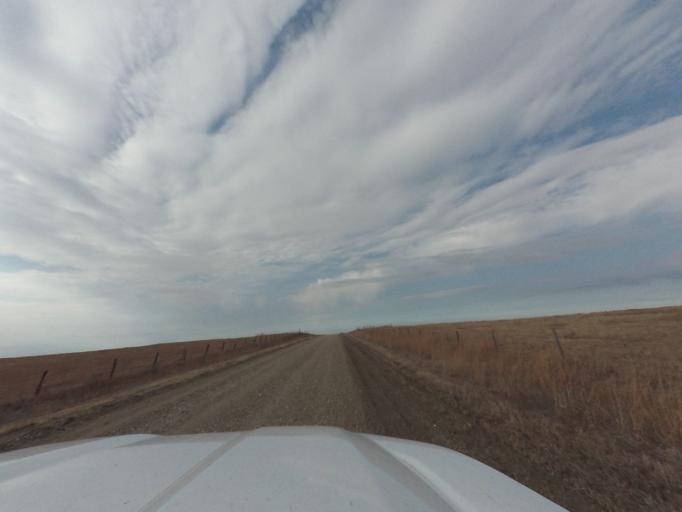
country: US
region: Kansas
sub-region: Chase County
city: Cottonwood Falls
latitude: 38.2171
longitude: -96.7001
